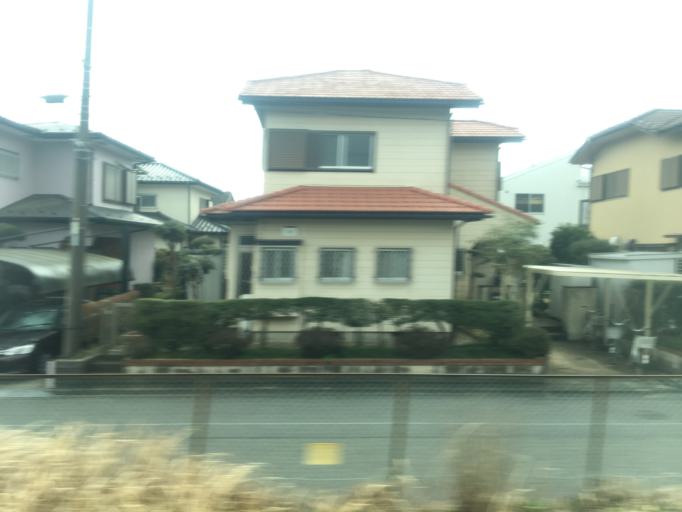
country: JP
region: Chiba
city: Narita
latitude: 35.8318
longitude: 140.2521
